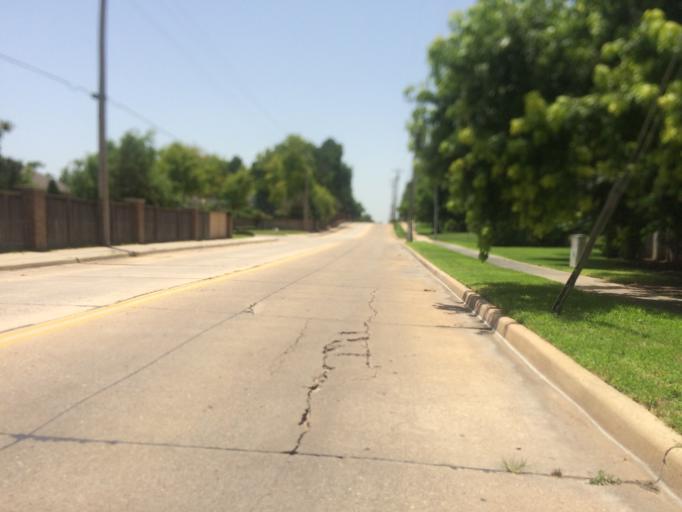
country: US
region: Oklahoma
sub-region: Cleveland County
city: Norman
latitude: 35.1894
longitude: -97.4596
